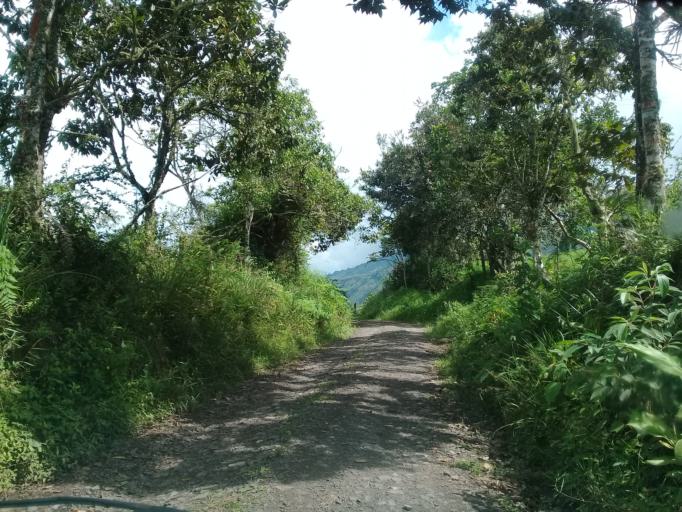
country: CO
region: Cundinamarca
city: Granada
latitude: 5.0995
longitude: -74.5648
